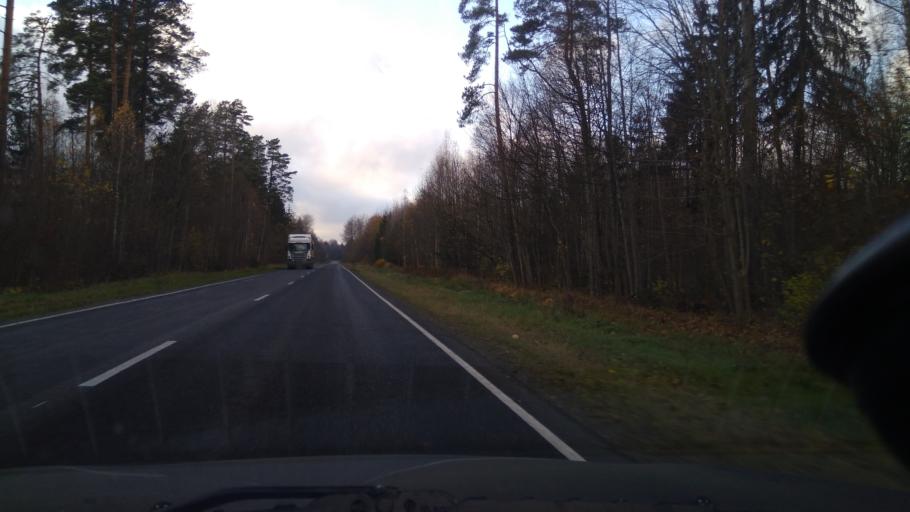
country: BY
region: Minsk
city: Urechcha
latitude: 53.2081
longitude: 27.9300
